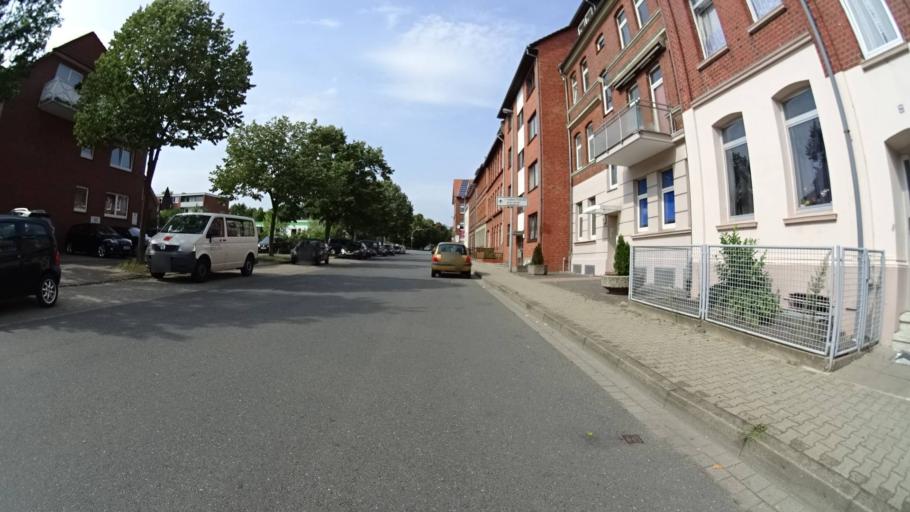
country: DE
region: Lower Saxony
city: Lueneburg
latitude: 53.2484
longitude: 10.3852
